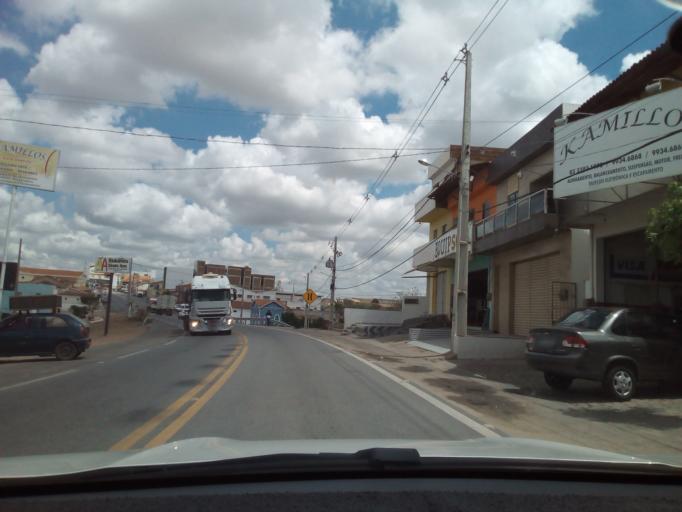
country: BR
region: Paraiba
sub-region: Soledade
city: Soledade
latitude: -7.0577
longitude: -36.3595
